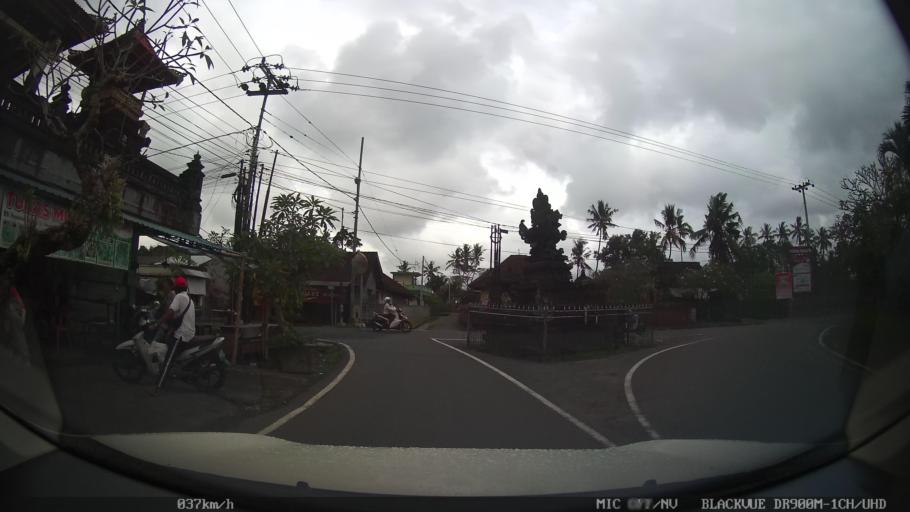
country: ID
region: Bali
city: Banjar Cemenggon
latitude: -8.5250
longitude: 115.1860
